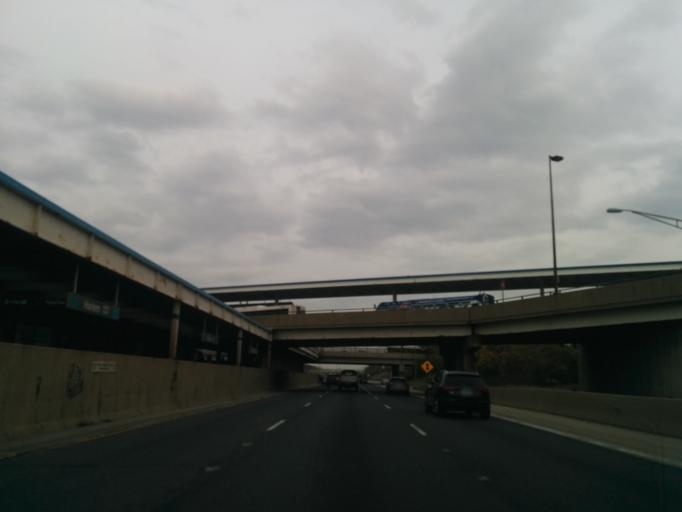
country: US
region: Illinois
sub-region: Cook County
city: Harwood Heights
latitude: 41.9822
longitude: -87.8090
